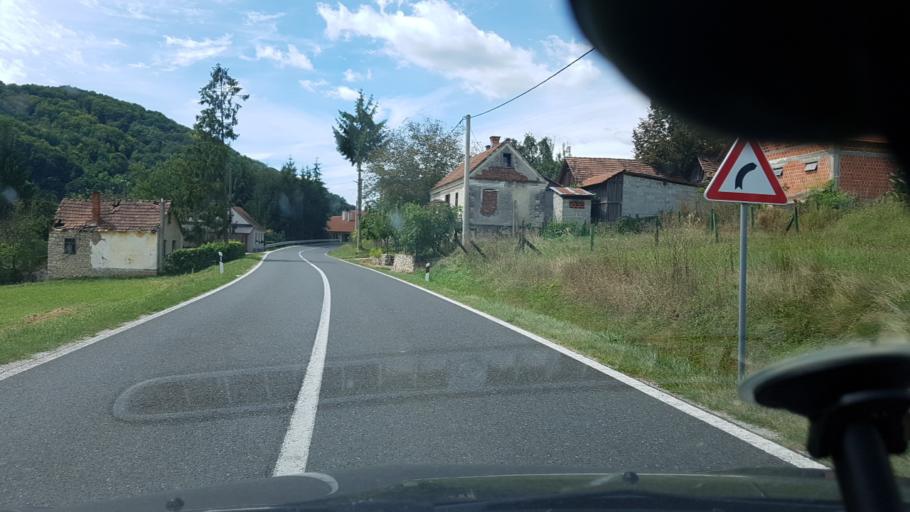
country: HR
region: Varazdinska
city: Lepoglava
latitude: 46.2131
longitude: 16.0152
